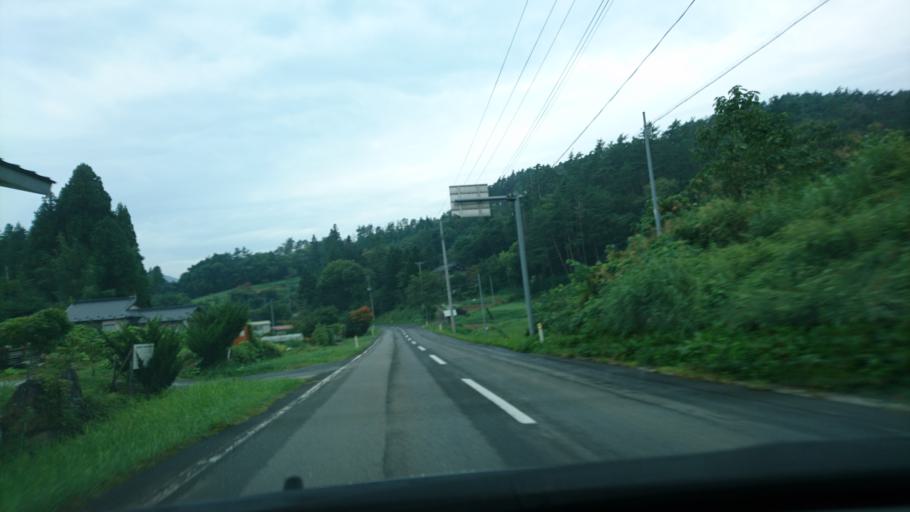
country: JP
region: Iwate
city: Ichinoseki
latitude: 39.0163
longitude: 141.2521
